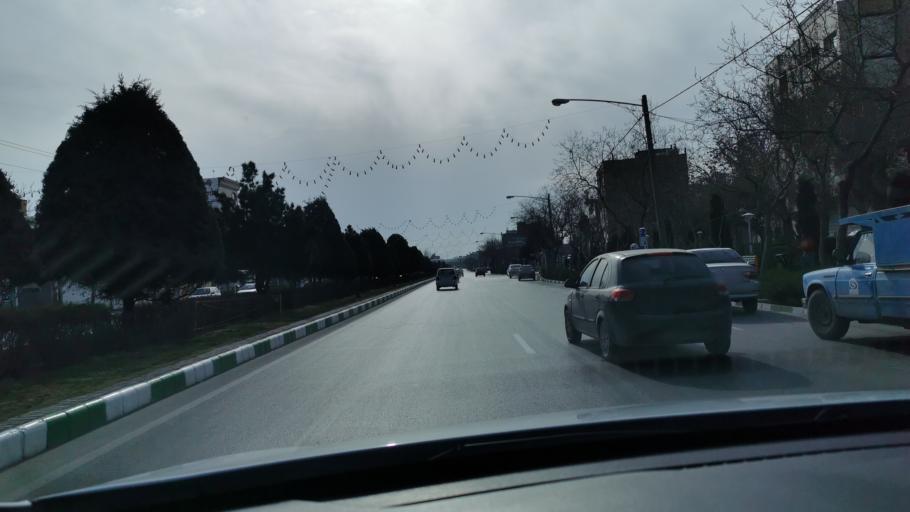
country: IR
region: Razavi Khorasan
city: Mashhad
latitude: 36.3039
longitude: 59.5143
